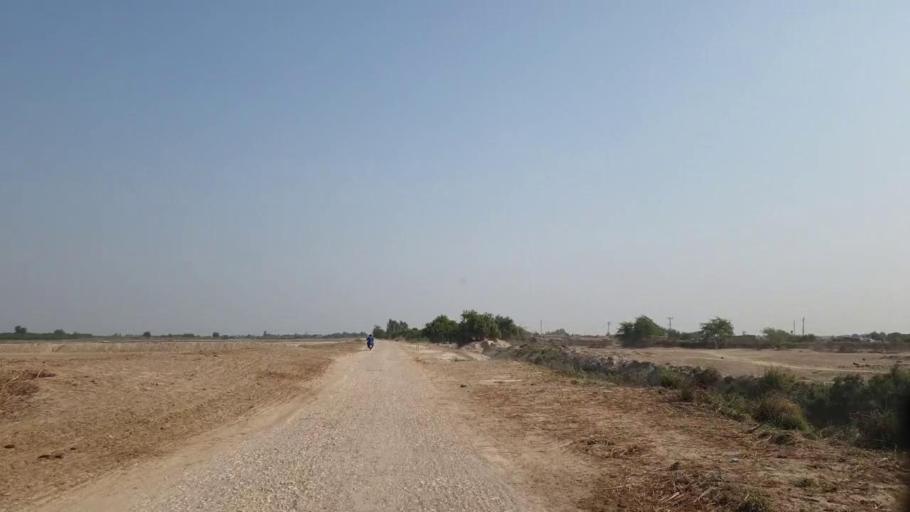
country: PK
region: Sindh
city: Bulri
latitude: 24.9356
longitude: 68.3623
